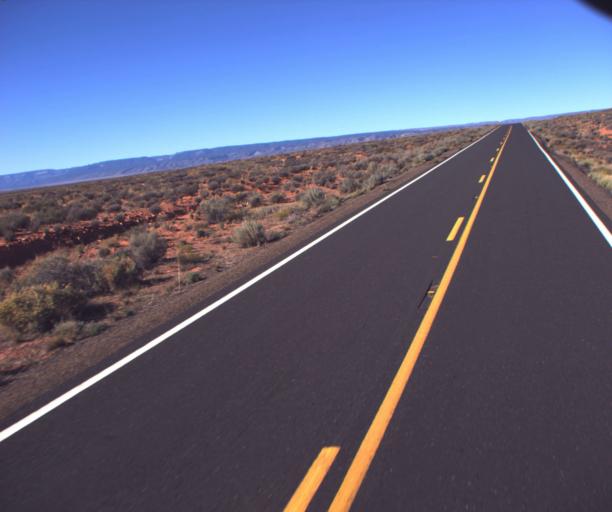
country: US
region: Arizona
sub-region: Coconino County
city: LeChee
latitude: 36.6869
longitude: -111.8297
